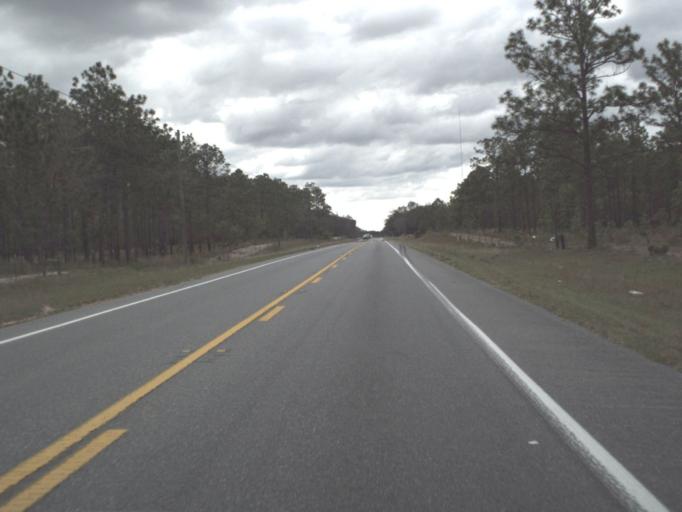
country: US
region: Florida
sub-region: Marion County
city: Ocala
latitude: 29.2463
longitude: -82.0593
